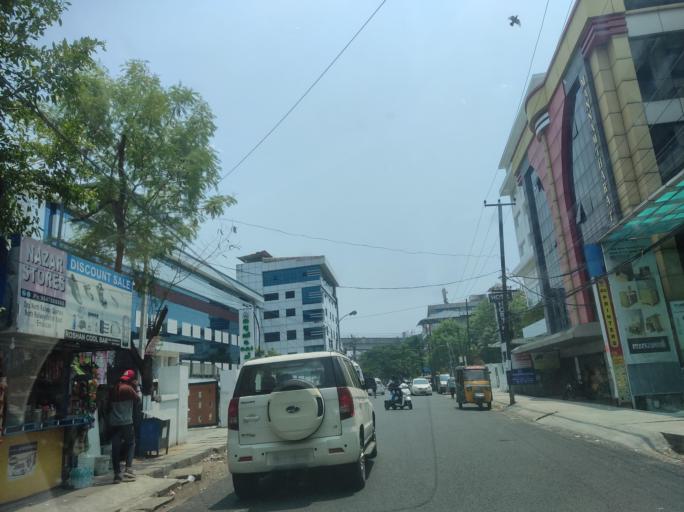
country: IN
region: Kerala
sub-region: Ernakulam
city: Cochin
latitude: 9.9899
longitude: 76.2851
